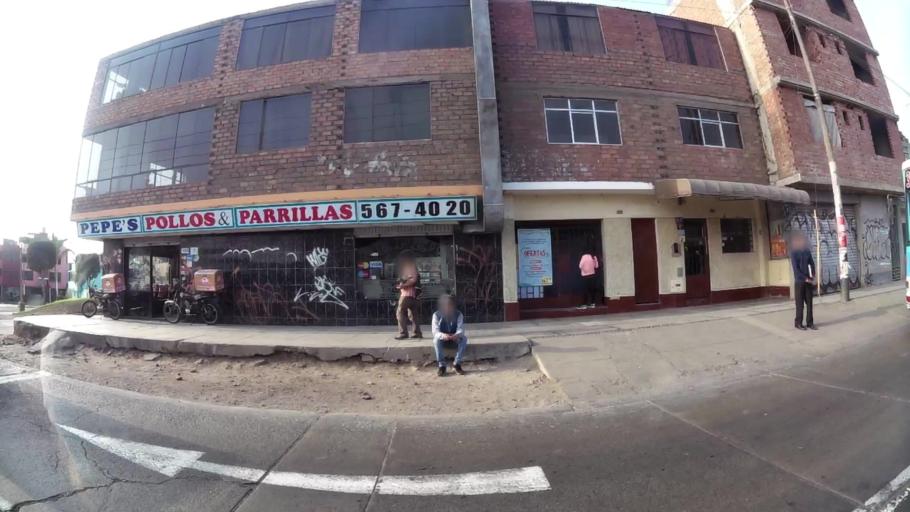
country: PE
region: Callao
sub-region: Callao
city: Callao
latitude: -12.0195
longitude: -77.0897
